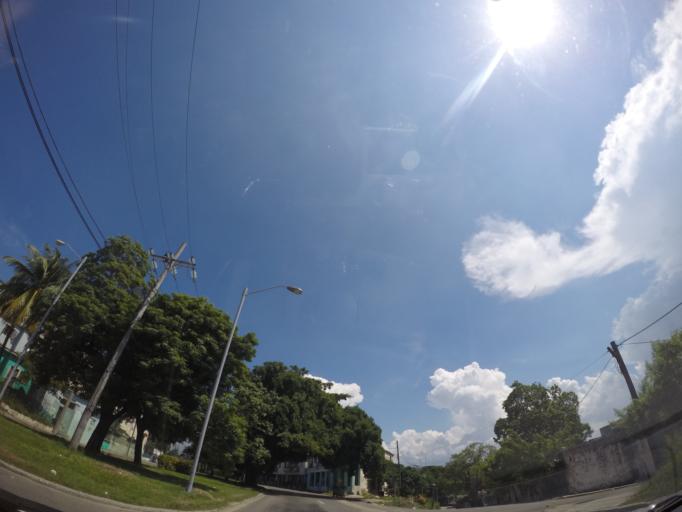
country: CU
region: La Habana
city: Havana
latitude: 23.1290
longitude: -82.3891
